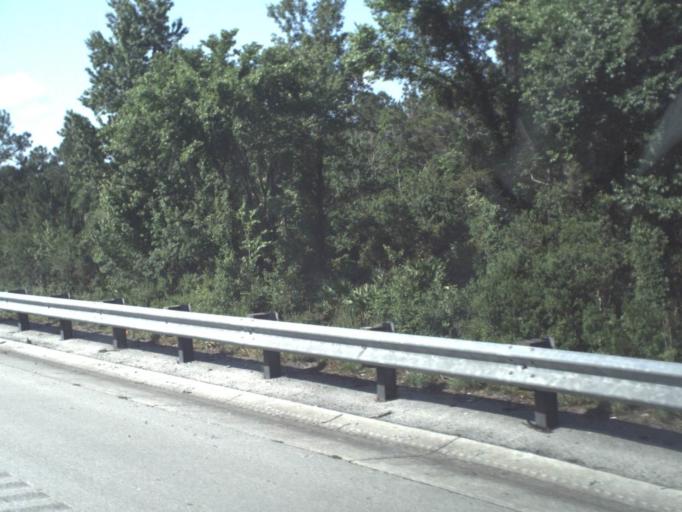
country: US
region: Florida
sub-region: Saint Johns County
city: Saint Augustine South
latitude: 29.8439
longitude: -81.3884
